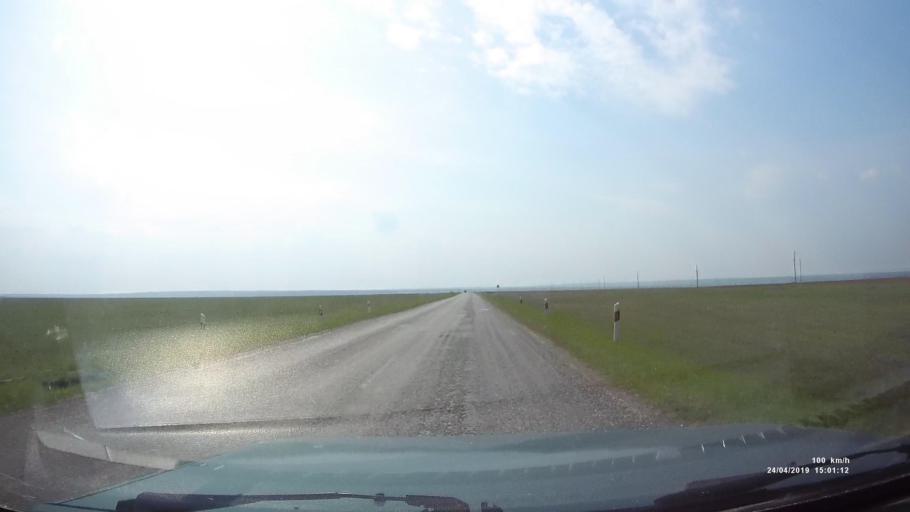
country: RU
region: Rostov
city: Remontnoye
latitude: 46.5656
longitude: 43.5388
